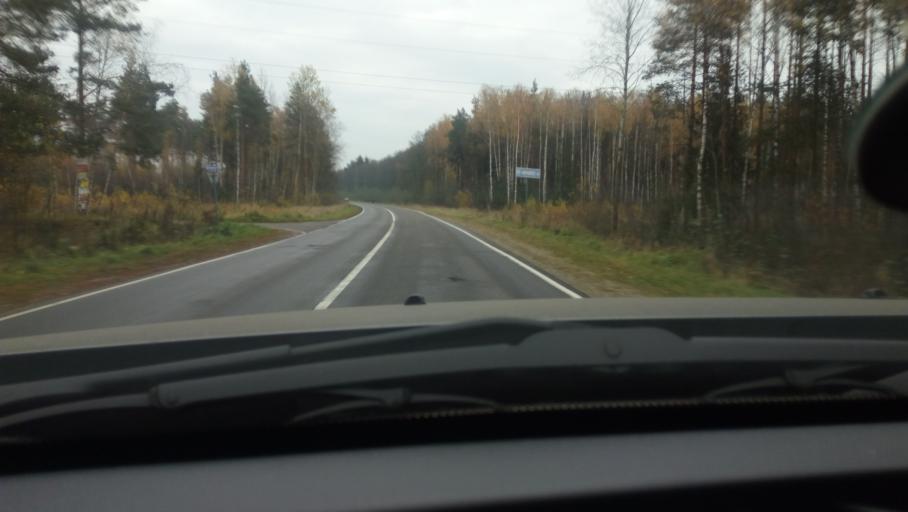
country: RU
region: Moskovskaya
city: Likino-Dulevo
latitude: 55.6973
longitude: 38.9092
